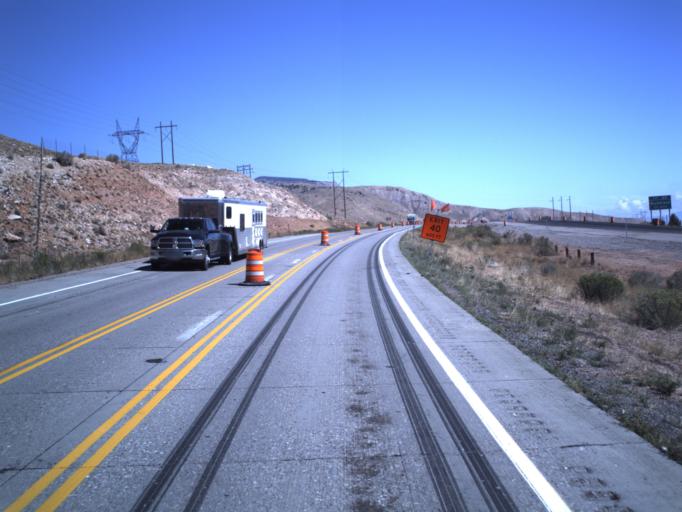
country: US
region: Utah
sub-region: Sevier County
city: Richfield
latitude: 38.7807
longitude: -112.0951
